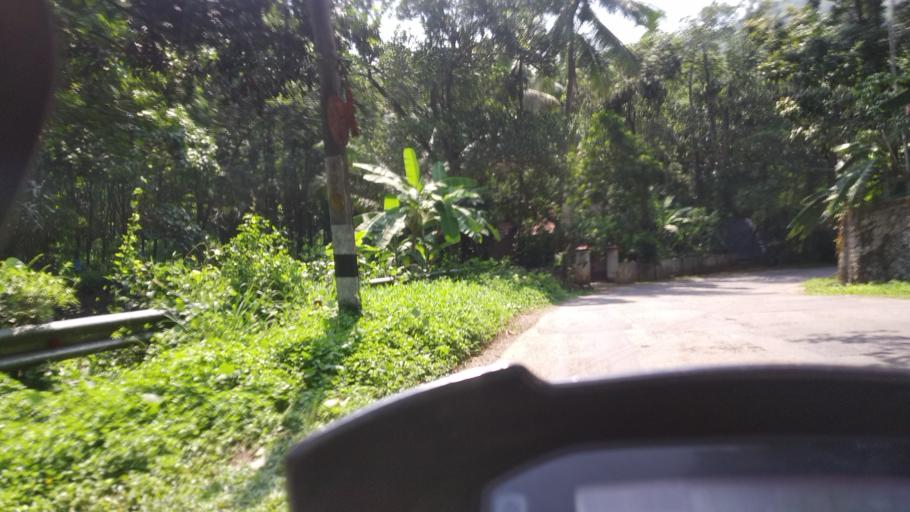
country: IN
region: Kerala
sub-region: Kottayam
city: Erattupetta
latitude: 9.6954
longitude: 76.8237
